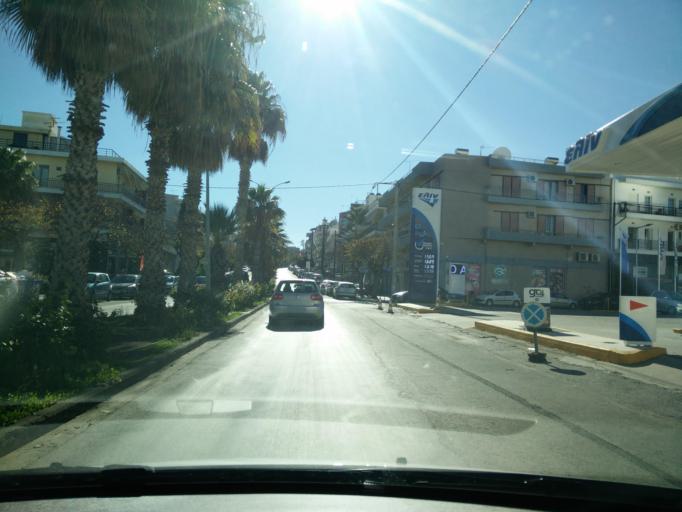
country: GR
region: Crete
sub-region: Nomos Irakleiou
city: Irakleion
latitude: 35.3380
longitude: 25.1419
